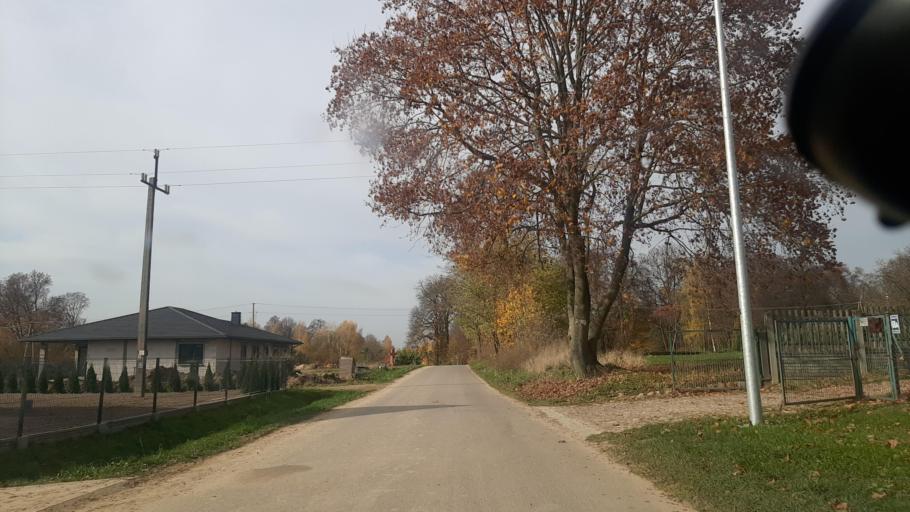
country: PL
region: Lublin Voivodeship
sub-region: Powiat lubelski
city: Jastkow
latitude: 51.3393
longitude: 22.4194
